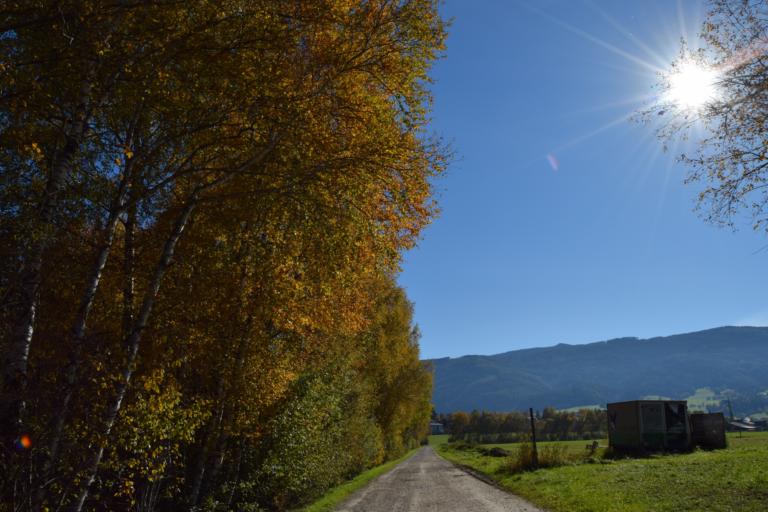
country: AT
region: Styria
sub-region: Politischer Bezirk Liezen
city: Irdning
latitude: 47.5125
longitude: 14.1048
